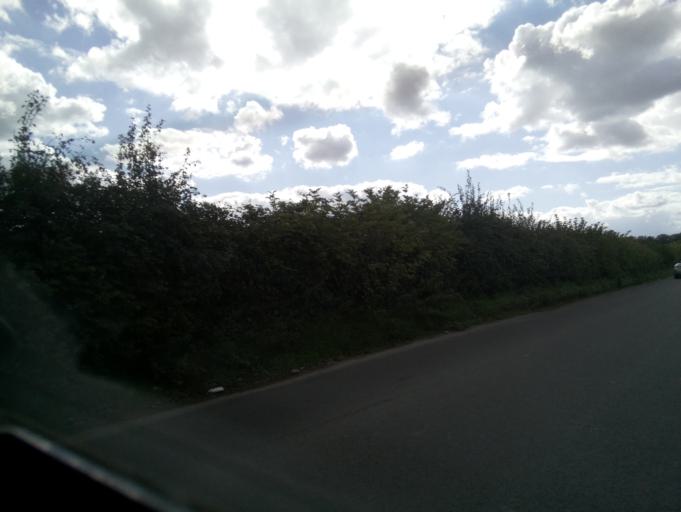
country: GB
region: England
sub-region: Wiltshire
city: Salisbury
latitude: 51.0936
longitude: -1.7942
